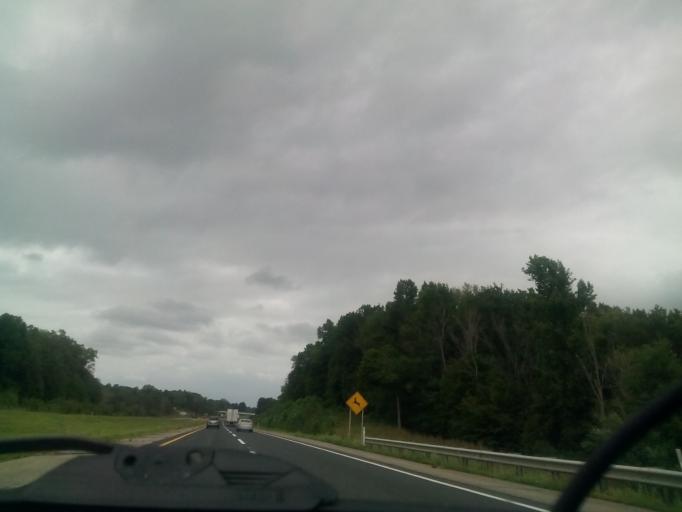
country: US
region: Indiana
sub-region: Steuben County
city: Fremont
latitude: 41.6449
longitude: -84.8384
